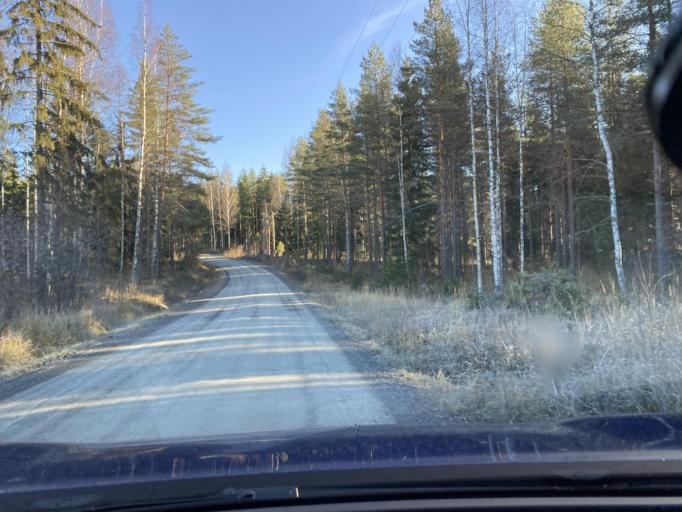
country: FI
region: Haeme
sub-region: Haemeenlinna
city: Kalvola
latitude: 60.9882
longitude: 24.0784
